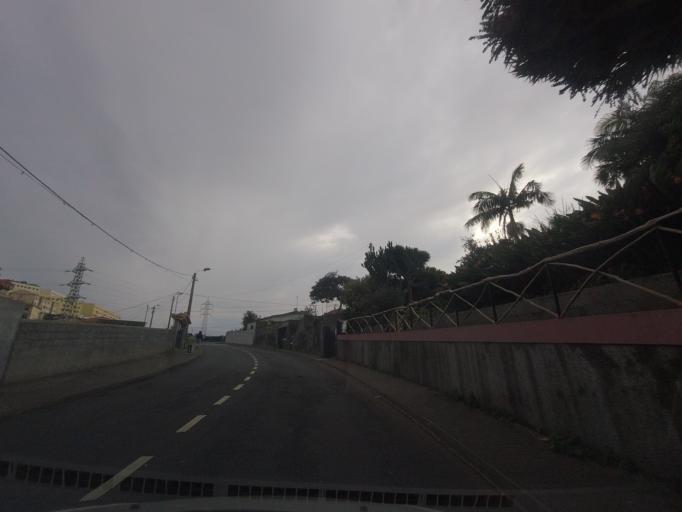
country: PT
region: Madeira
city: Camara de Lobos
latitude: 32.6674
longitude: -16.9487
